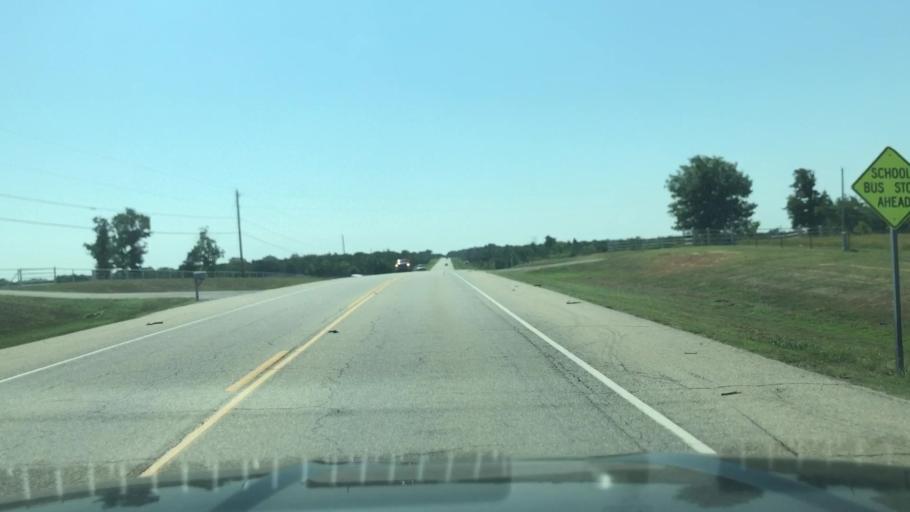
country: US
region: Oklahoma
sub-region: Creek County
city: Mannford
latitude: 35.9973
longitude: -96.3618
